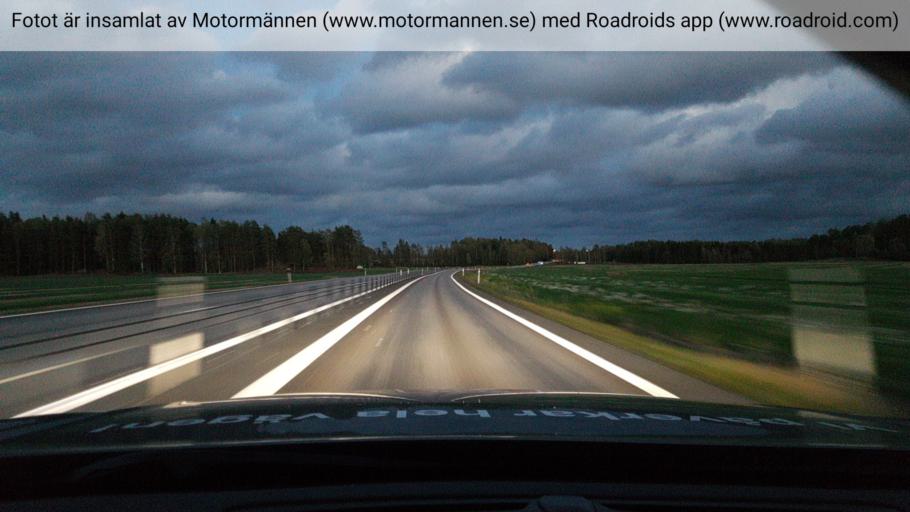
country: SE
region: Vaermland
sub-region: Kristinehamns Kommun
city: Kristinehamn
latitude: 59.3736
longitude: 13.9962
